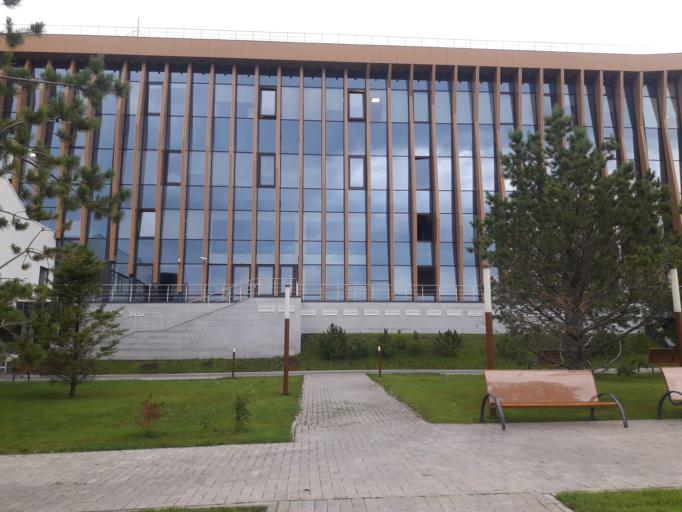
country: RU
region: Tatarstan
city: Sviyazhsk
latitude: 55.7536
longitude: 48.7419
